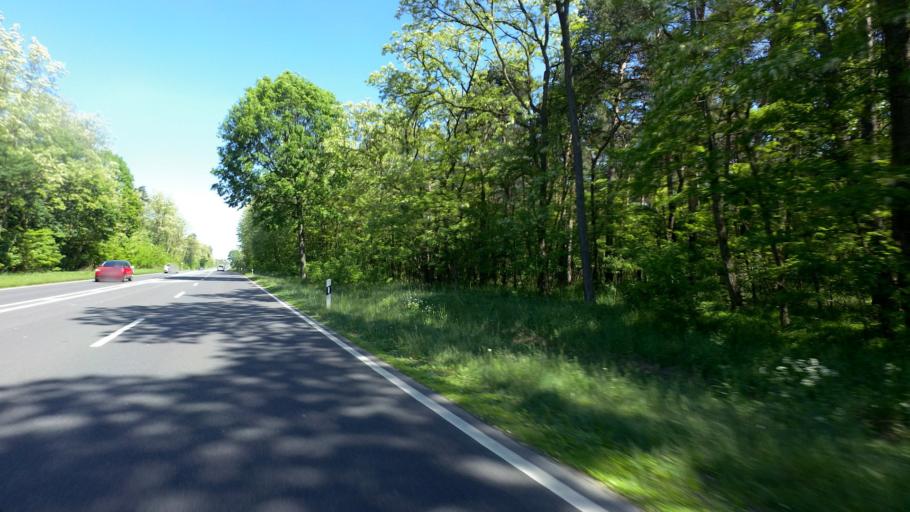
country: DE
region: Brandenburg
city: Spremberg
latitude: 51.6199
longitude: 14.3629
